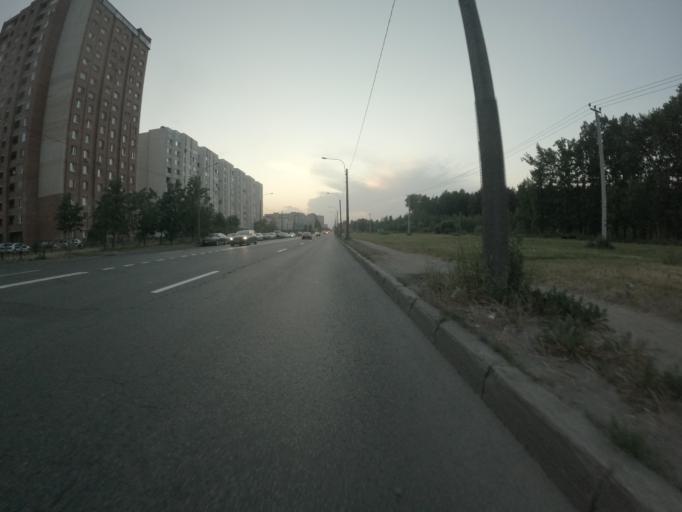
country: RU
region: St.-Petersburg
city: Krasnogvargeisky
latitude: 59.9485
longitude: 30.5029
